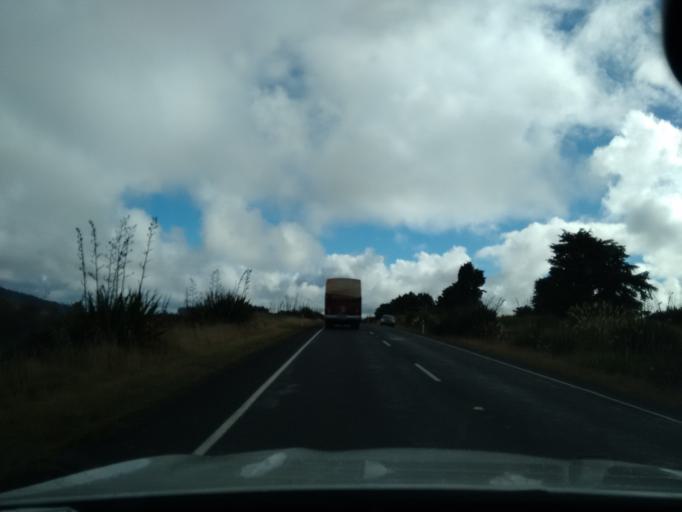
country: NZ
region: Manawatu-Wanganui
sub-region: Ruapehu District
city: Waiouru
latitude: -39.1830
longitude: 175.4405
